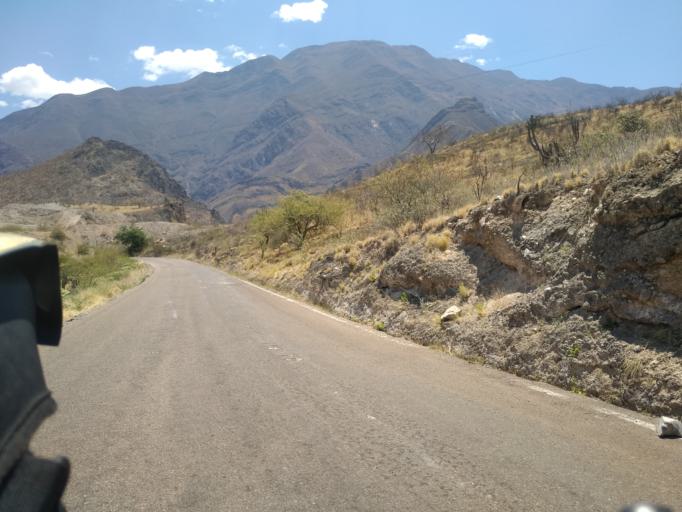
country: PE
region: Amazonas
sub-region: Provincia de Chachapoyas
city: Balsas
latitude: -6.8473
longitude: -78.0384
